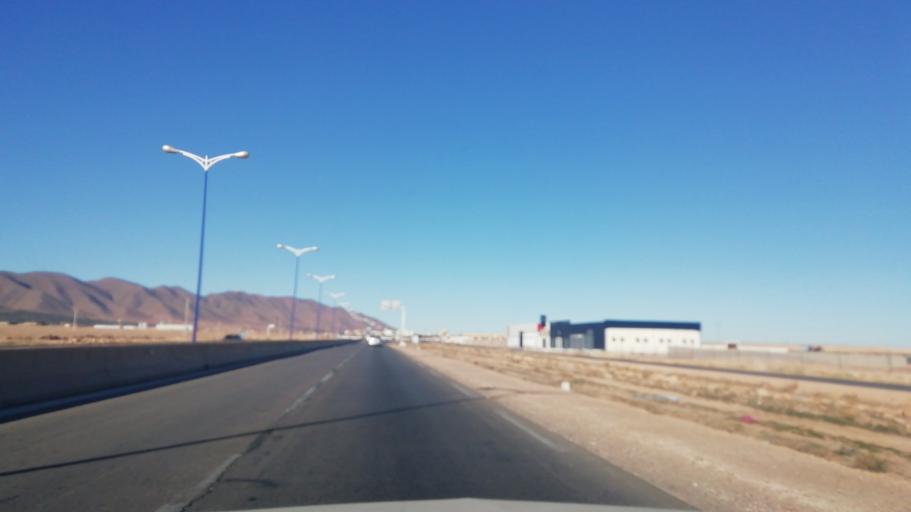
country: DZ
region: Wilaya de Naama
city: Naama
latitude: 33.5064
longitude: -0.2874
